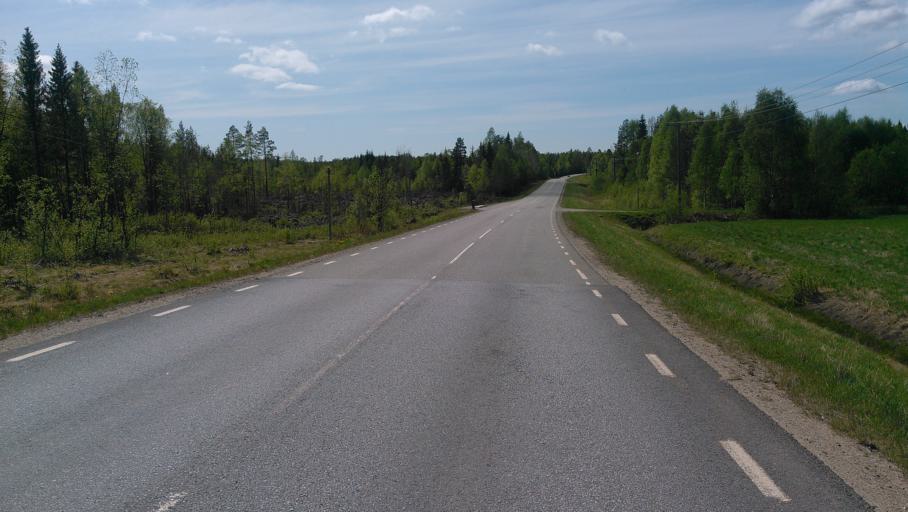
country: SE
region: Vaesterbotten
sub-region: Vannas Kommun
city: Vannasby
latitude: 63.8568
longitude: 19.9994
